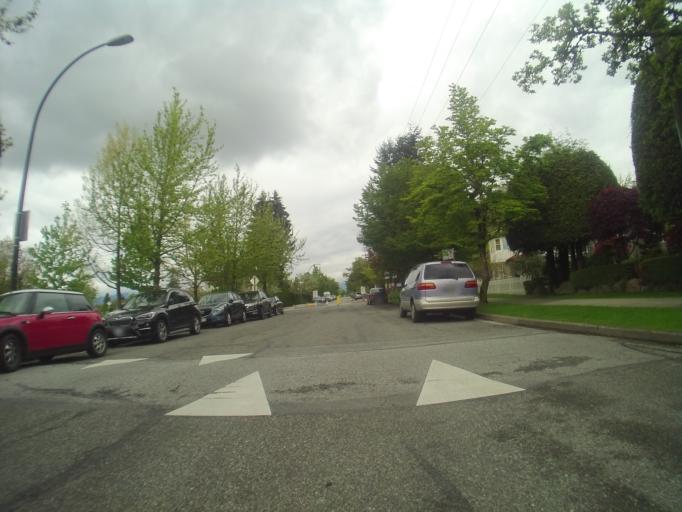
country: CA
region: British Columbia
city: Vancouver
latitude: 49.2439
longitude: -123.1052
